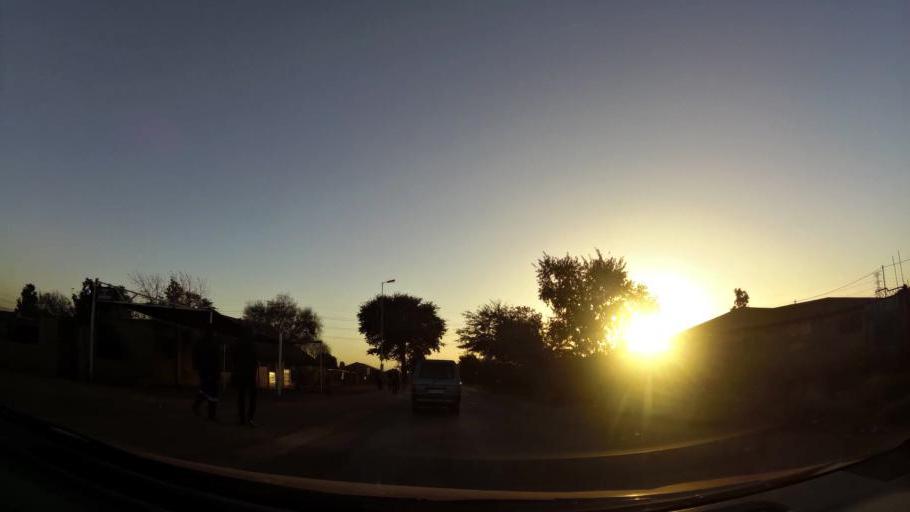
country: ZA
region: Gauteng
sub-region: City of Tshwane Metropolitan Municipality
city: Mabopane
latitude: -25.5816
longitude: 28.0772
